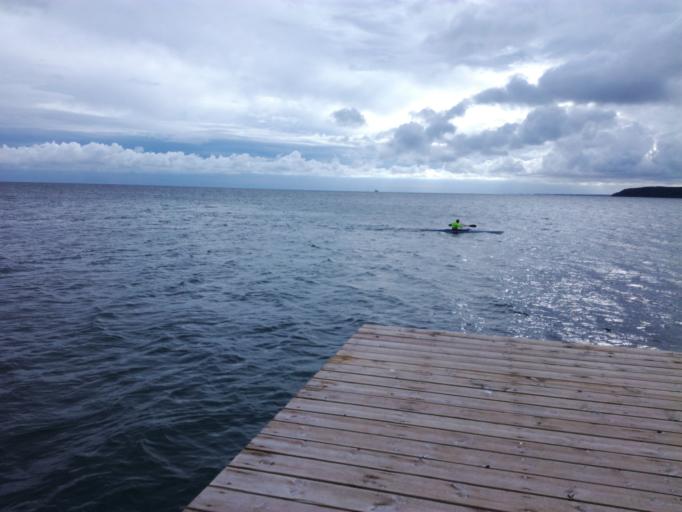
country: DK
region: South Denmark
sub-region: Fredericia Kommune
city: Fredericia
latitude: 55.5632
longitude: 9.7696
